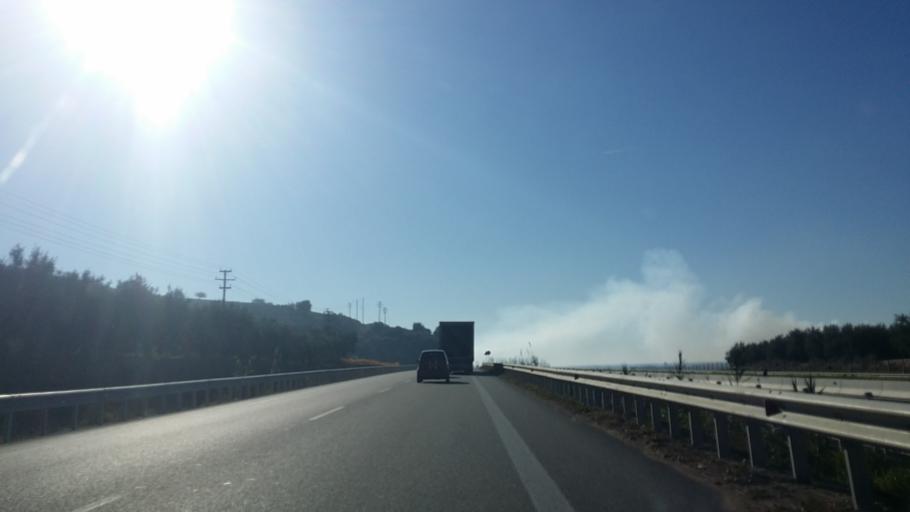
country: GR
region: West Greece
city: Aitoliko
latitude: 38.4212
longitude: 21.3884
